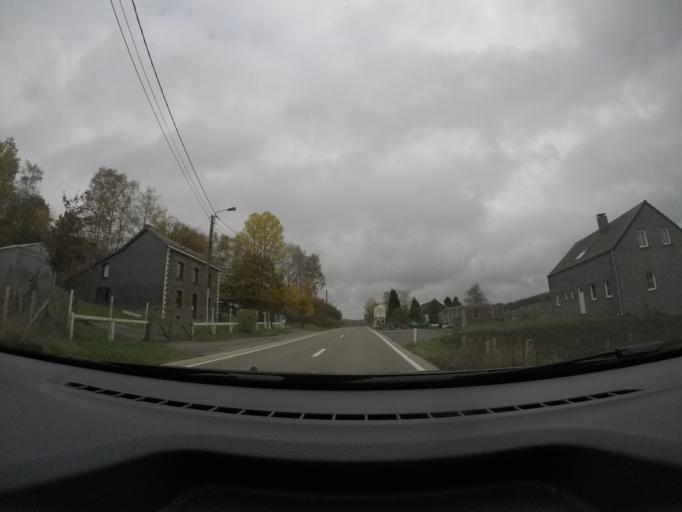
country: BE
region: Wallonia
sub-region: Province du Luxembourg
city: Bertogne
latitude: 50.0890
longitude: 5.7158
